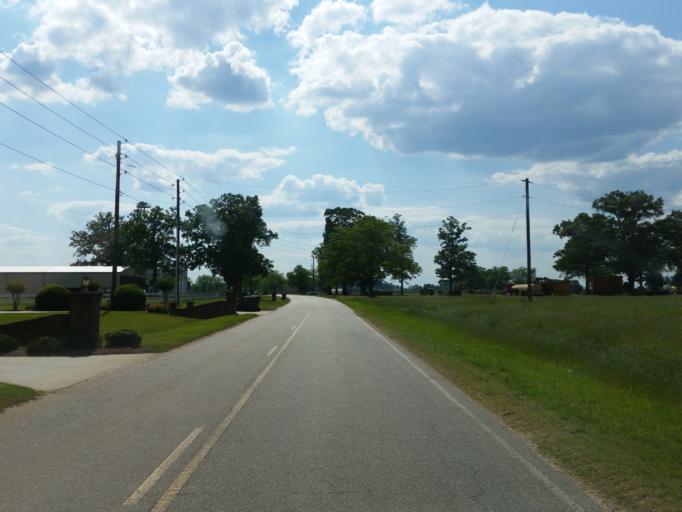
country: US
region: Georgia
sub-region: Houston County
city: Centerville
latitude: 32.5784
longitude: -83.7267
